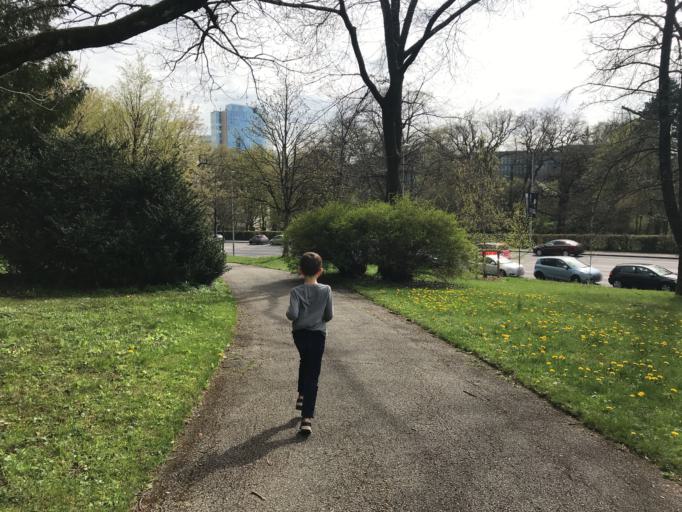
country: CH
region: Geneva
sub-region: Geneva
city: Le Grand-Saconnex
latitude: 46.2246
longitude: 6.1376
